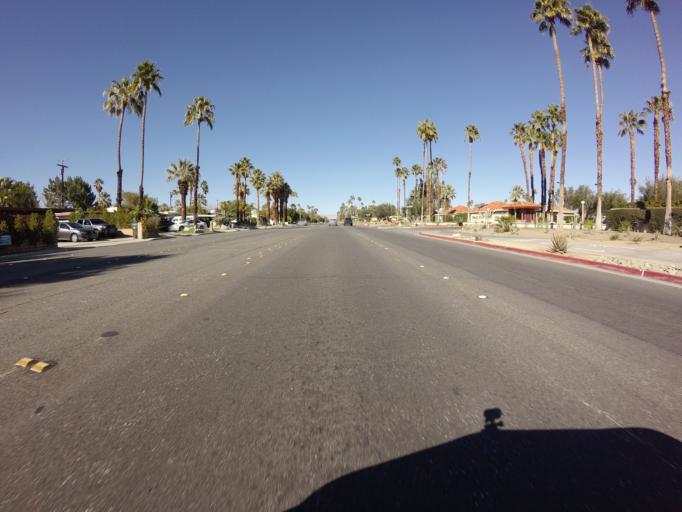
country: US
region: California
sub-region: Riverside County
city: Palm Springs
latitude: 33.8329
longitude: -116.5282
